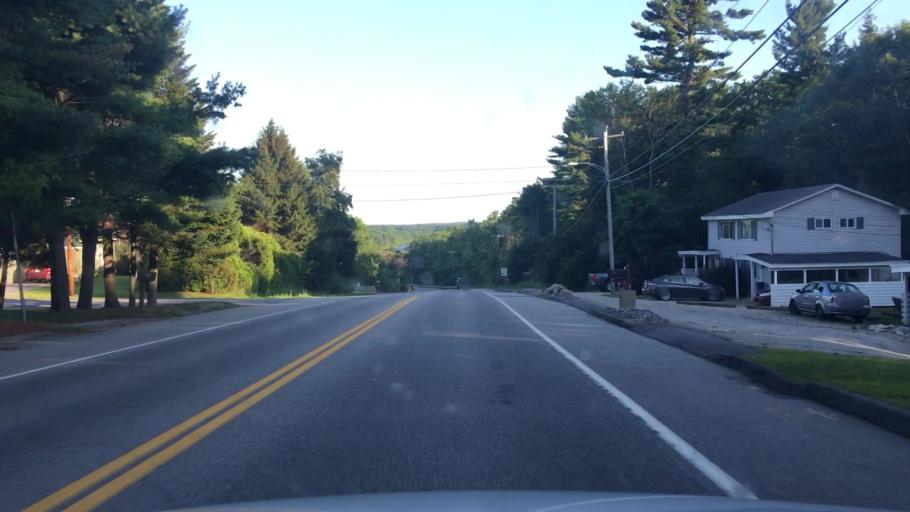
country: US
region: Maine
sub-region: Androscoggin County
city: Lisbon
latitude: 44.0157
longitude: -70.0915
